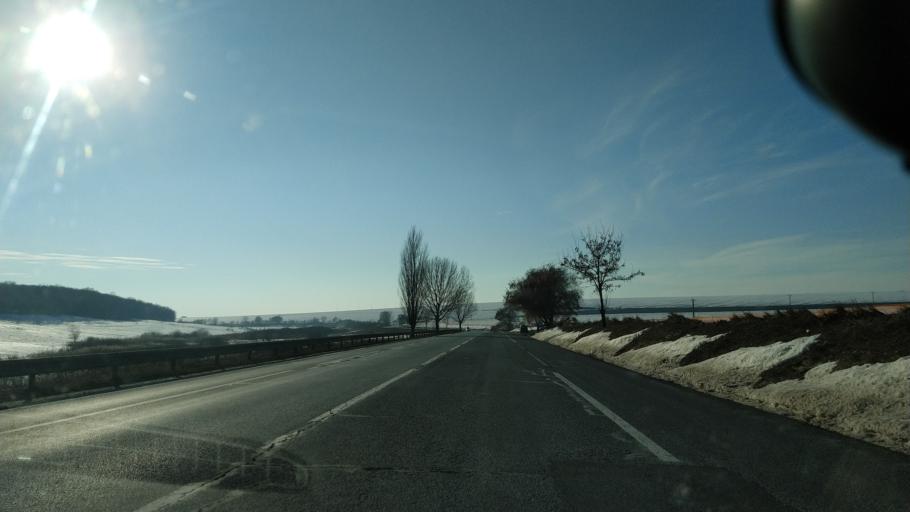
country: RO
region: Iasi
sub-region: Comuna Strunga
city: Strunga
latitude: 47.1343
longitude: 26.9452
